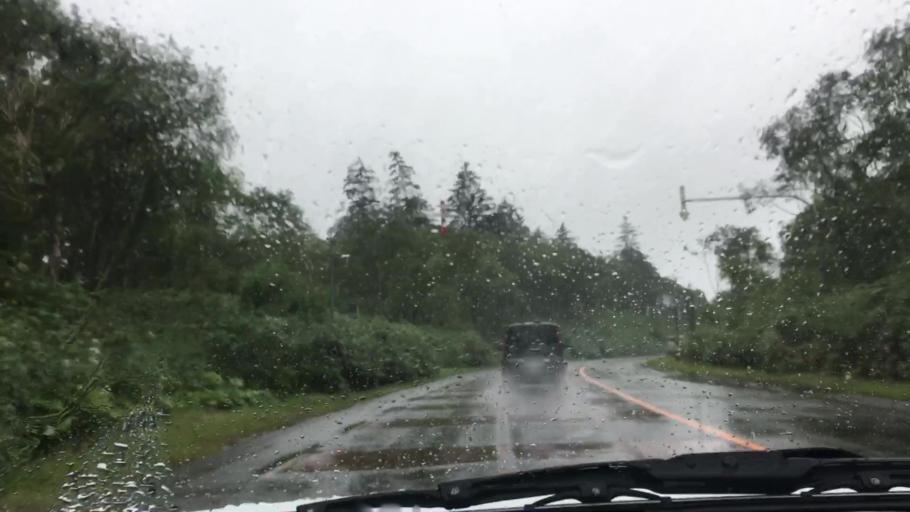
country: JP
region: Hokkaido
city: Sapporo
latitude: 42.8661
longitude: 141.1100
